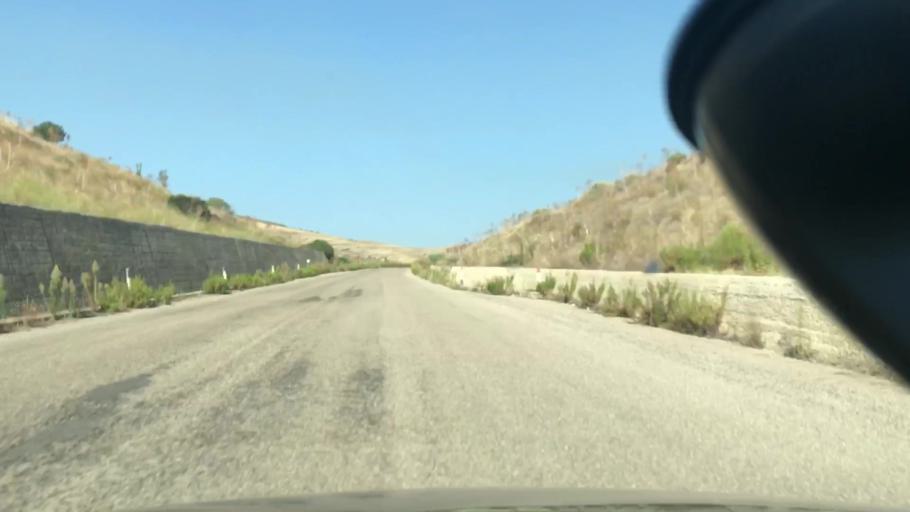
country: IT
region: Basilicate
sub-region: Provincia di Matera
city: Grottole
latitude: 40.6935
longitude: 16.4313
